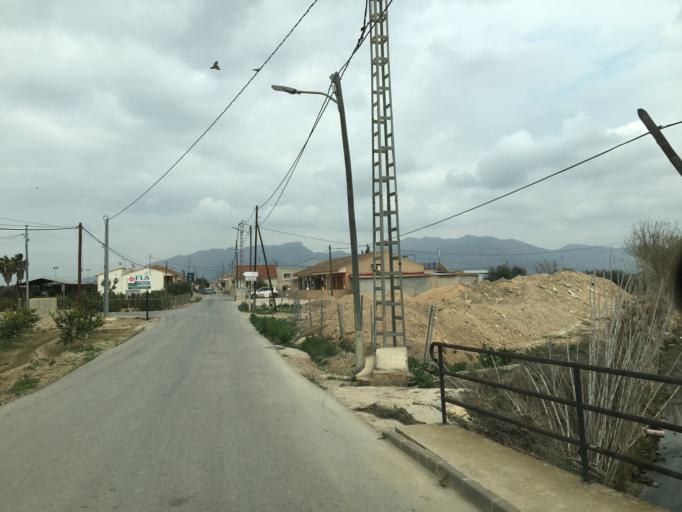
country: ES
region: Murcia
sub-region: Murcia
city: Beniel
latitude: 38.0319
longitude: -0.9828
